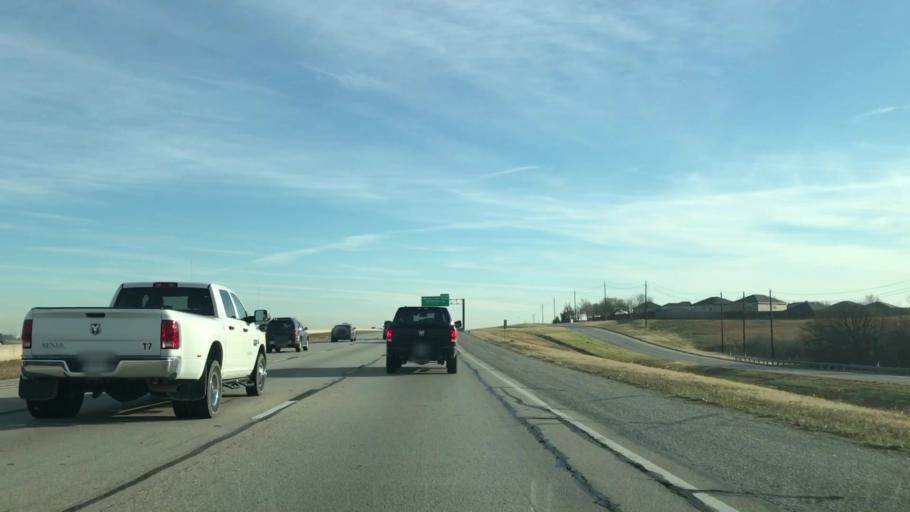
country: US
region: Texas
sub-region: Tarrant County
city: Sansom Park
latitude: 32.8181
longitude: -97.4022
